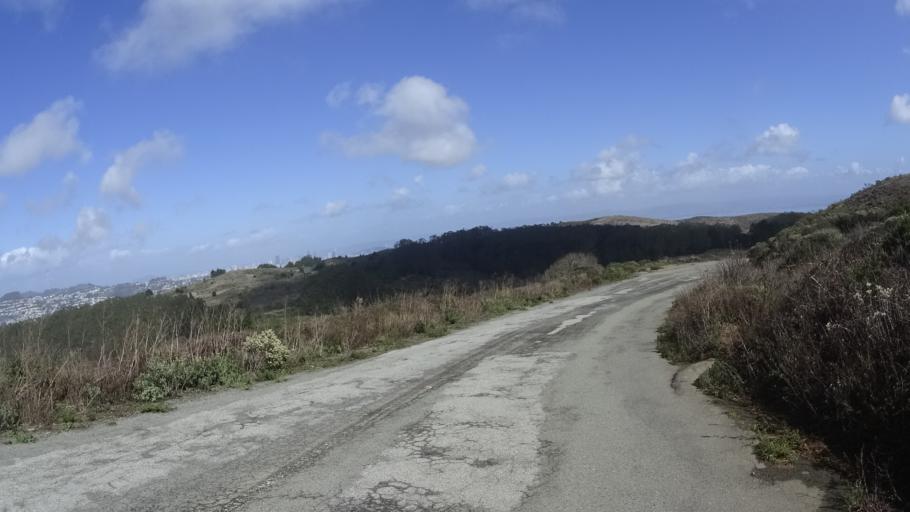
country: US
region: California
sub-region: San Mateo County
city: Daly City
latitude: 37.6950
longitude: -122.4419
